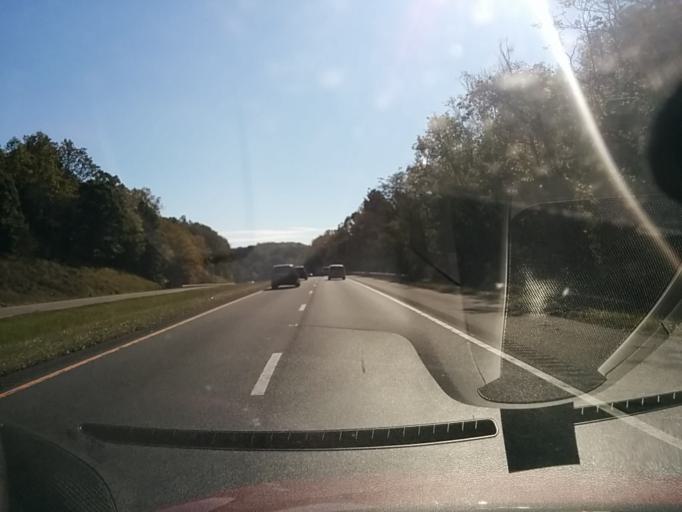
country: US
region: Virginia
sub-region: City of Charlottesville
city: Charlottesville
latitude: 38.0252
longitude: -78.5840
